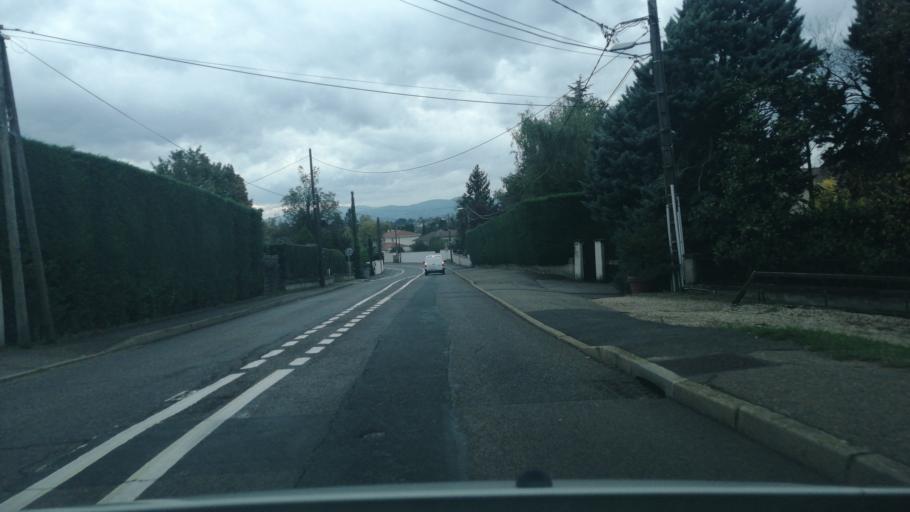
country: FR
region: Rhone-Alpes
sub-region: Departement du Rhone
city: Limonest
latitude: 45.8315
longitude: 4.7704
